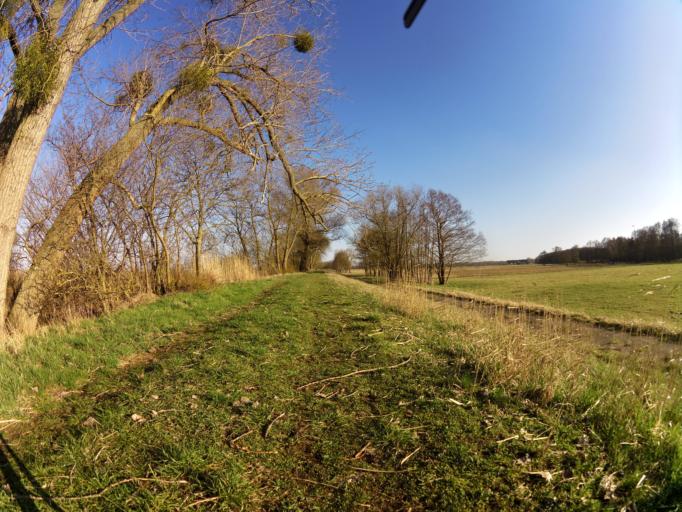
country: PL
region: West Pomeranian Voivodeship
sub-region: Powiat policki
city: Nowe Warpno
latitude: 53.7089
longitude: 14.3517
